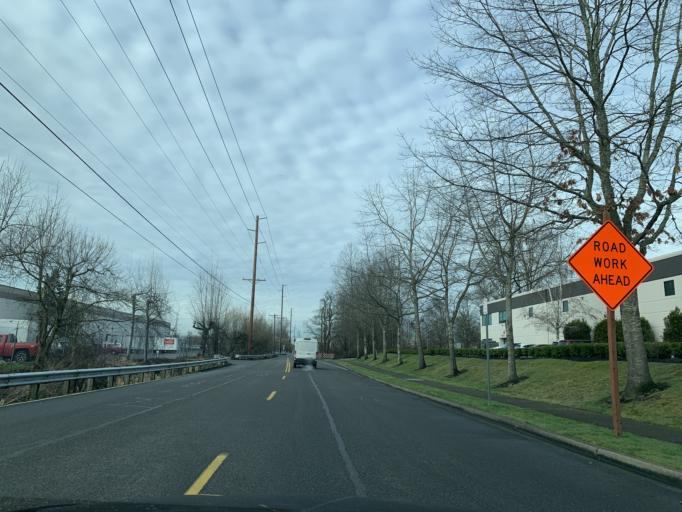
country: US
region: Washington
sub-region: Pierce County
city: Fife
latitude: 47.2500
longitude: -122.3533
